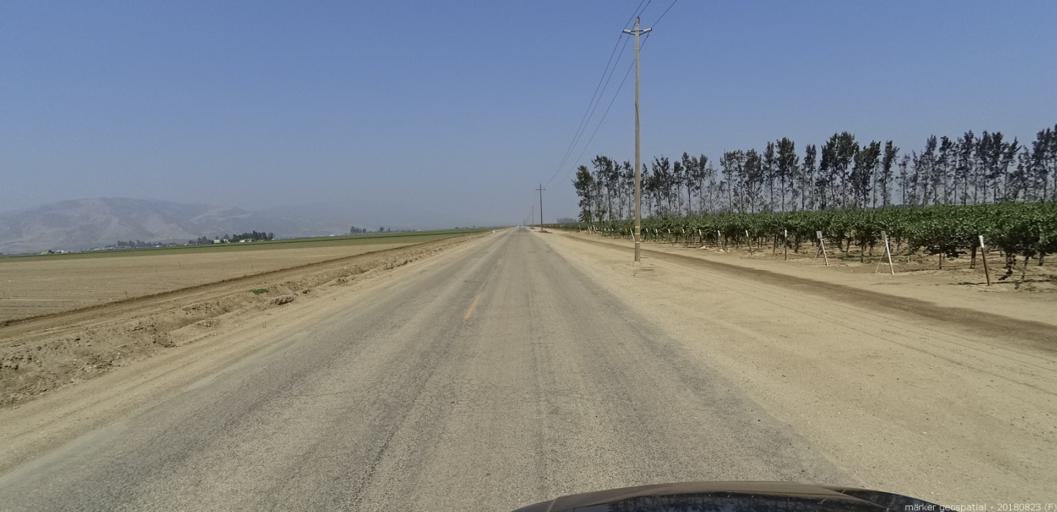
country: US
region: California
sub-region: Monterey County
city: Greenfield
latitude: 36.2928
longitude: -121.2555
